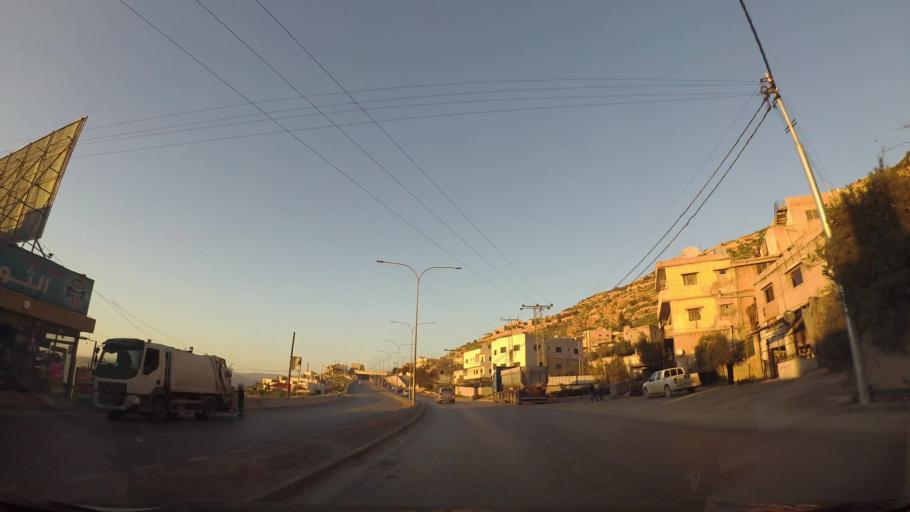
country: JO
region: Amman
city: Umm as Summaq
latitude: 31.8628
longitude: 35.7618
